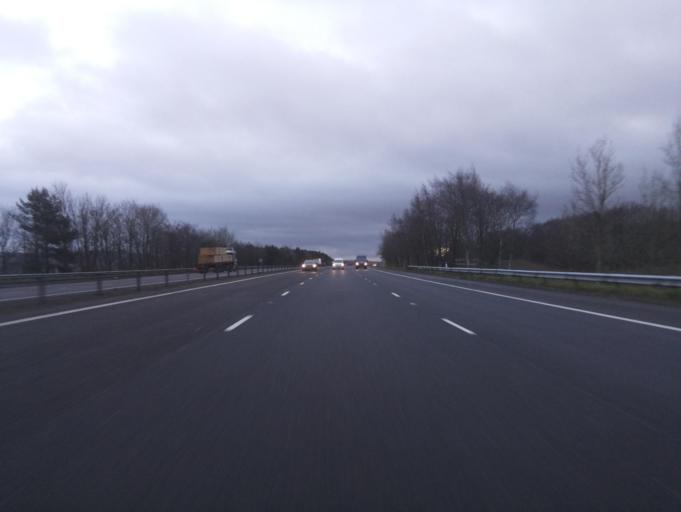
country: GB
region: Scotland
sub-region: Dumfries and Galloway
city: Moffat
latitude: 55.2726
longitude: -3.4199
